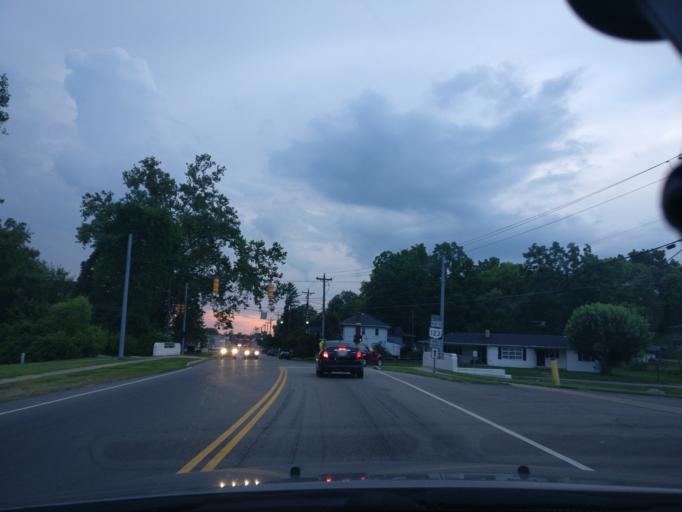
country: US
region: Ohio
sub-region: Warren County
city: Franklin
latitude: 39.5552
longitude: -84.3003
